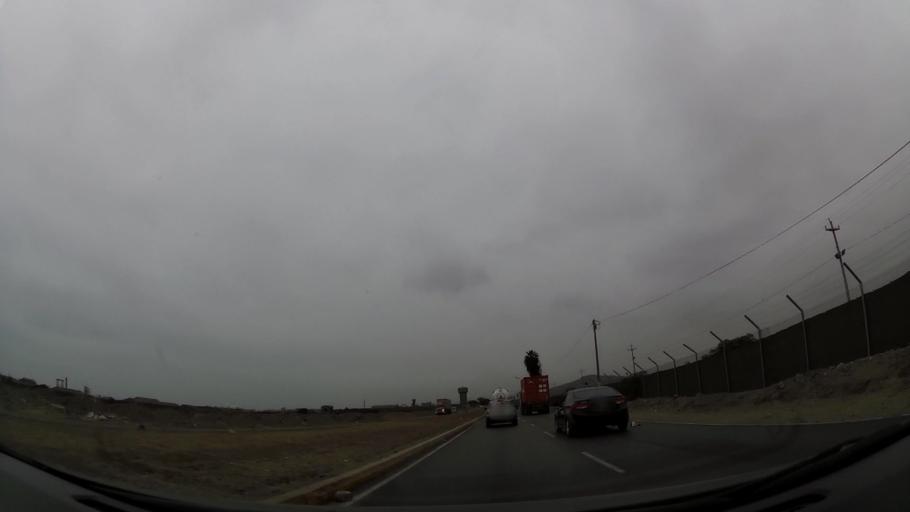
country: PE
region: Callao
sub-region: Callao
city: Callao
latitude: -12.0111
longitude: -77.1284
